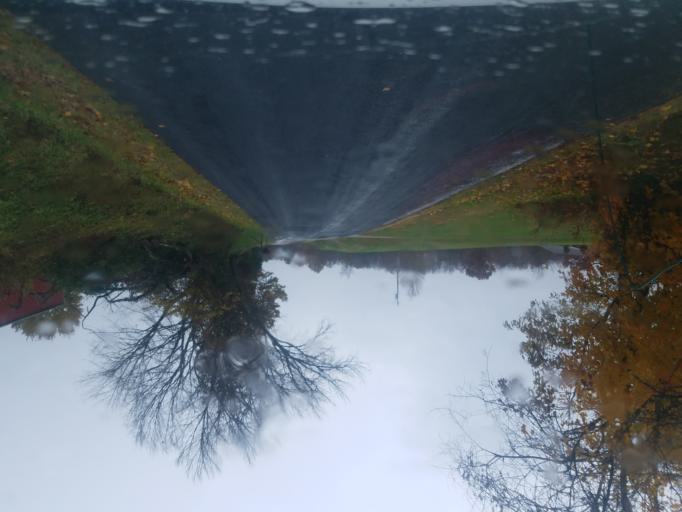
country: US
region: West Virginia
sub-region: Wood County
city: Blennerhassett
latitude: 39.3362
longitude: -81.6281
